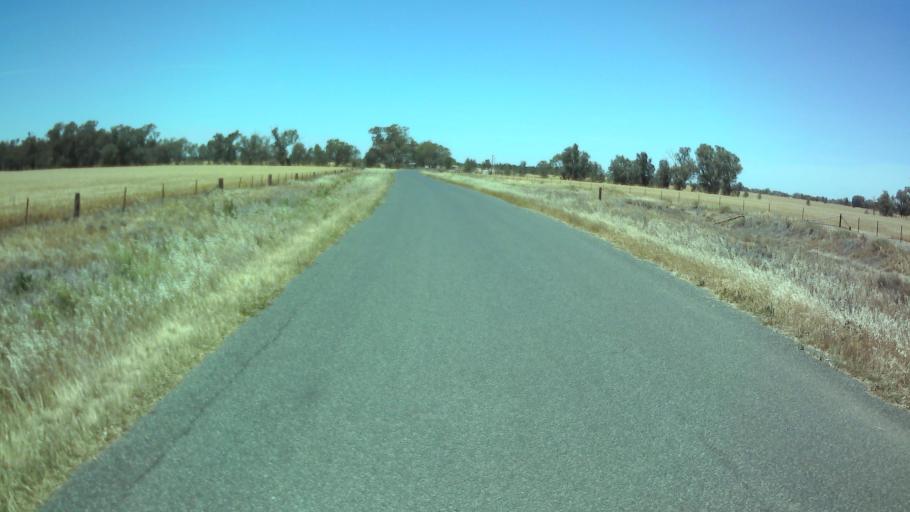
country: AU
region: New South Wales
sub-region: Weddin
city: Grenfell
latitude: -34.0363
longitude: 147.7898
